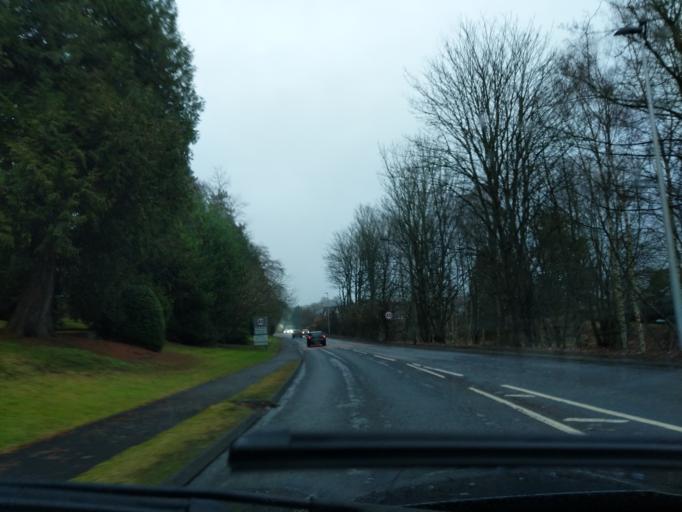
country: GB
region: Scotland
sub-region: The Scottish Borders
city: Melrose
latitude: 55.6026
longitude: -2.7434
